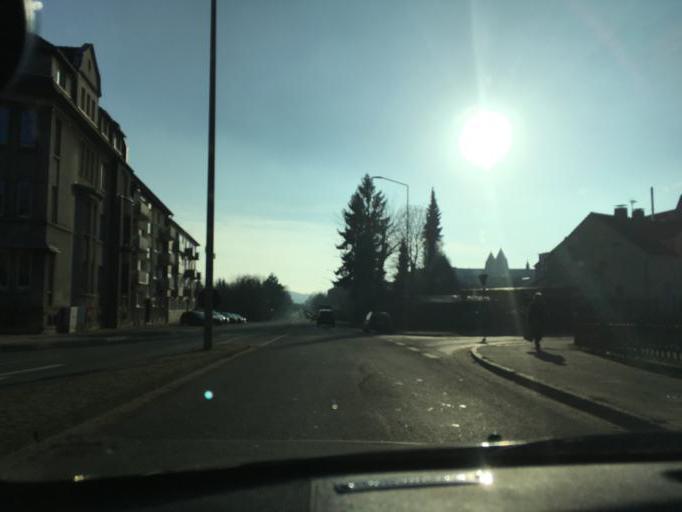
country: DE
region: North Rhine-Westphalia
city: Schwerte
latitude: 51.4457
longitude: 7.5648
